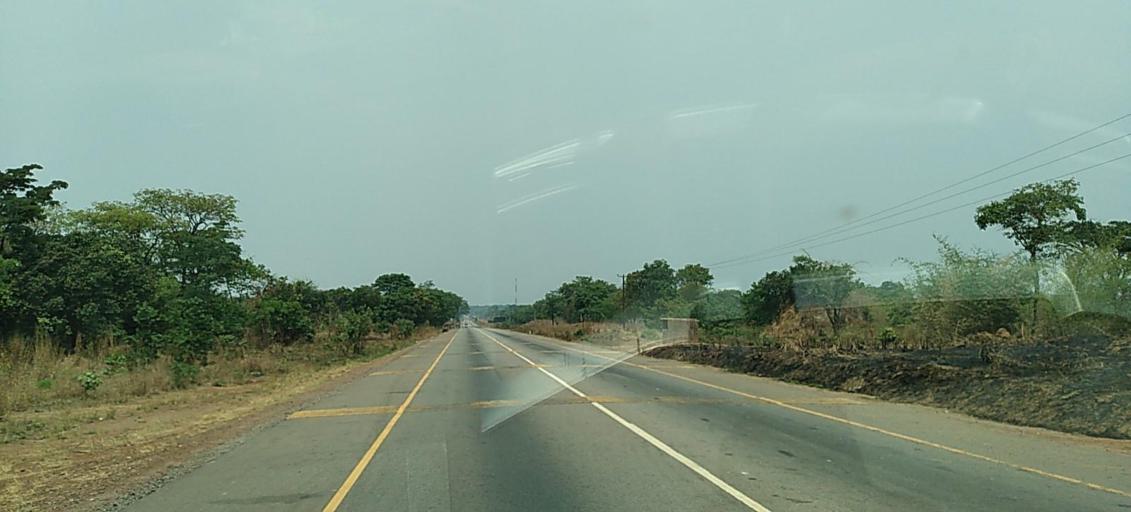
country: ZM
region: Copperbelt
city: Chingola
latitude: -12.5530
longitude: 27.7051
